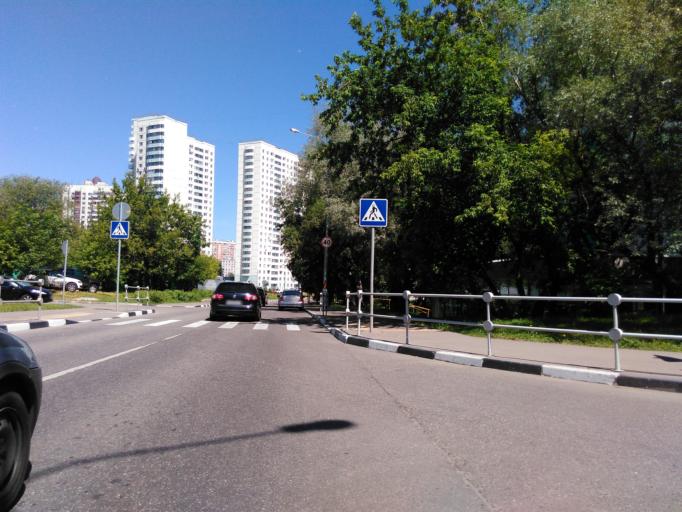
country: RU
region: Moskovskaya
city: Cheremushki
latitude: 55.6609
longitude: 37.5644
